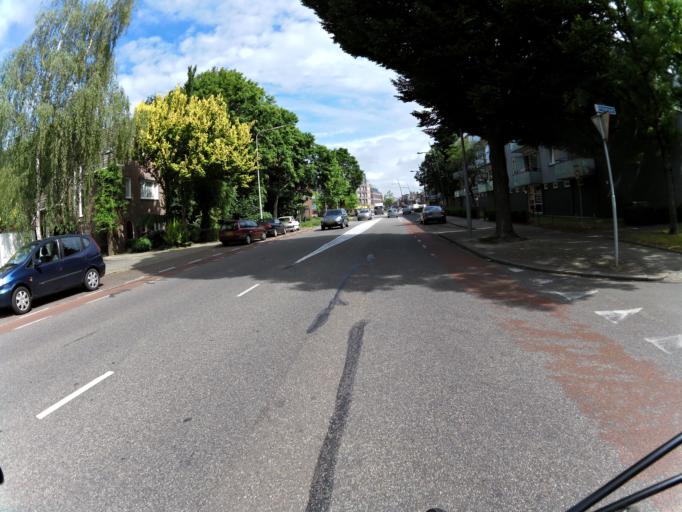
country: NL
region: Limburg
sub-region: Gemeente Heerlen
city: Heerlen
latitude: 50.8901
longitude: 6.0147
